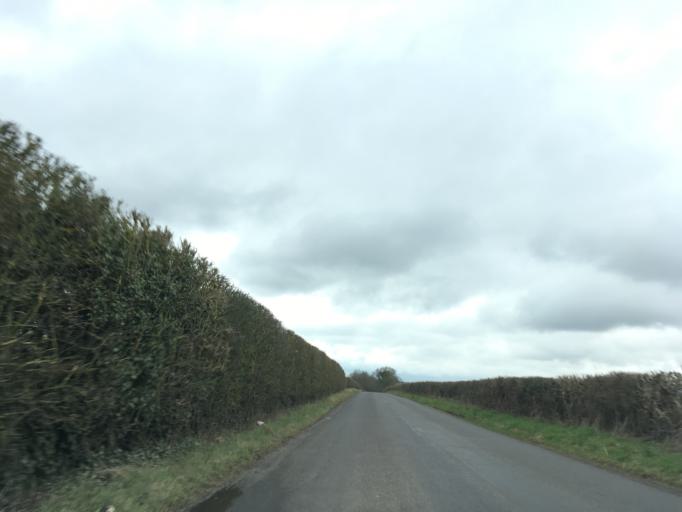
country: GB
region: England
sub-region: Wiltshire
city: Chilton Foliat
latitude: 51.4441
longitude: -1.5366
